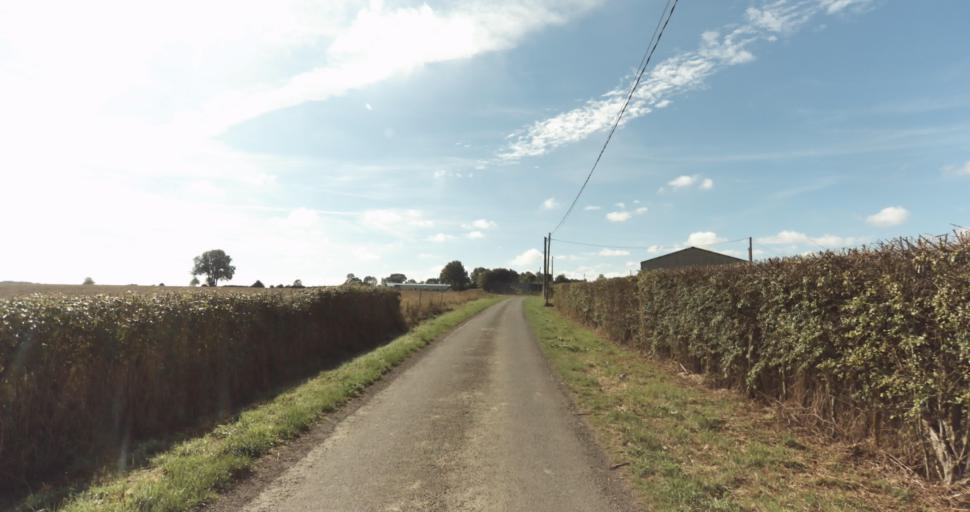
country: FR
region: Lower Normandy
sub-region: Departement du Calvados
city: La Vespiere
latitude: 48.9383
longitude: 0.3511
